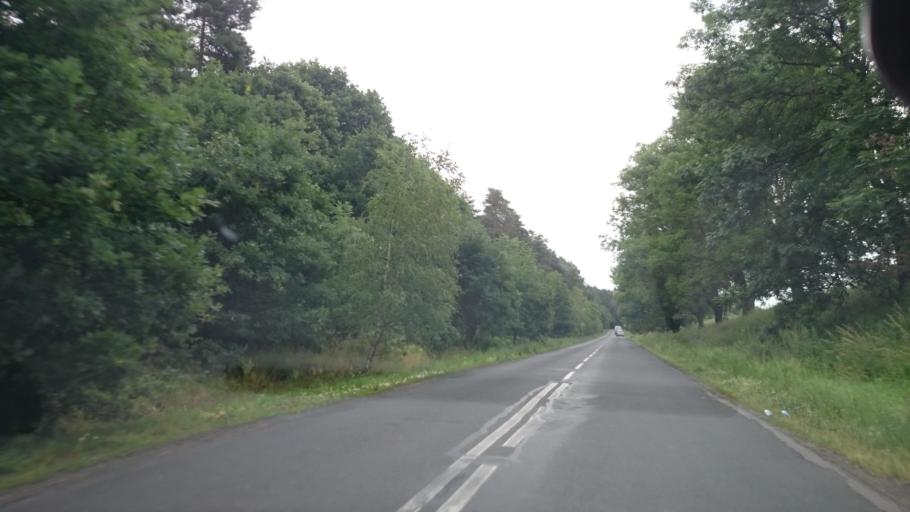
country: PL
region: Opole Voivodeship
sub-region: Powiat nyski
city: Sidzina
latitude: 50.6396
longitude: 17.5104
